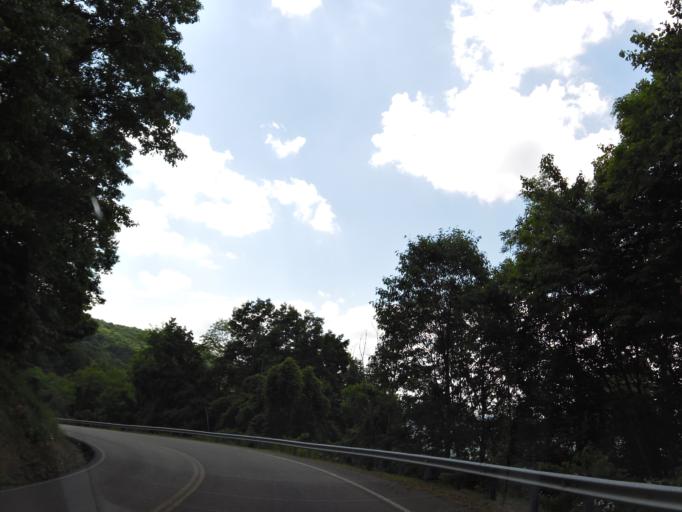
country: US
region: Tennessee
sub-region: Bledsoe County
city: Pikeville
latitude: 35.5925
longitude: -85.1384
